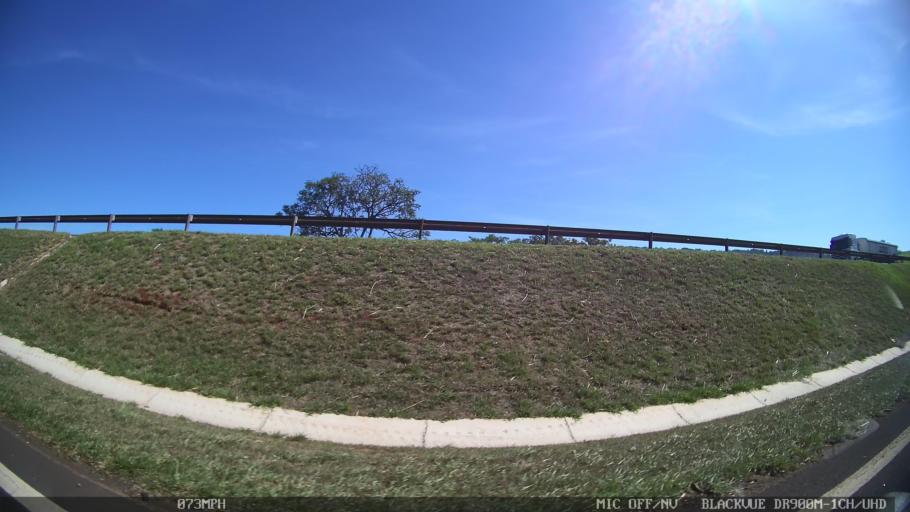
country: BR
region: Sao Paulo
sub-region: Sao Simao
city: Sao Simao
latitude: -21.5014
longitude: -47.6418
